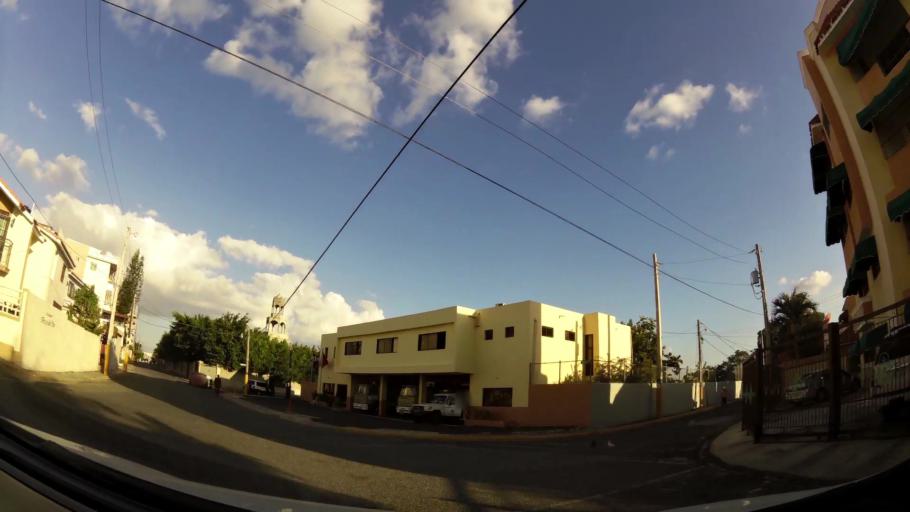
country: DO
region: Santo Domingo
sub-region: Santo Domingo
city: Santo Domingo Este
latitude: 18.4781
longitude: -69.8324
